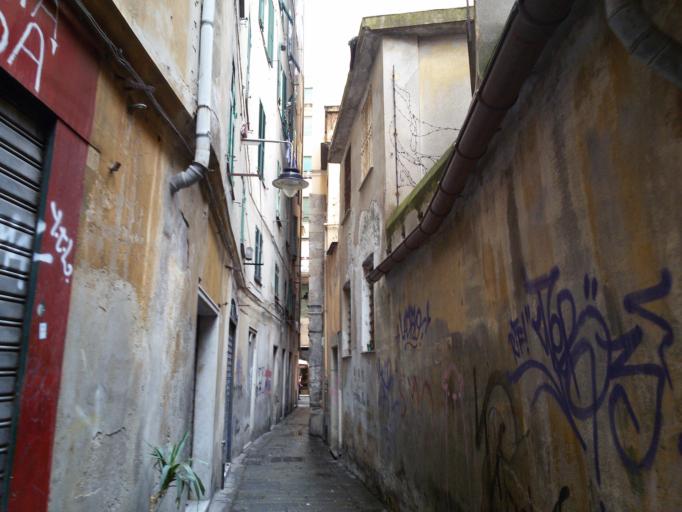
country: IT
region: Liguria
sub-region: Provincia di Genova
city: San Teodoro
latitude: 44.4097
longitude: 8.9319
